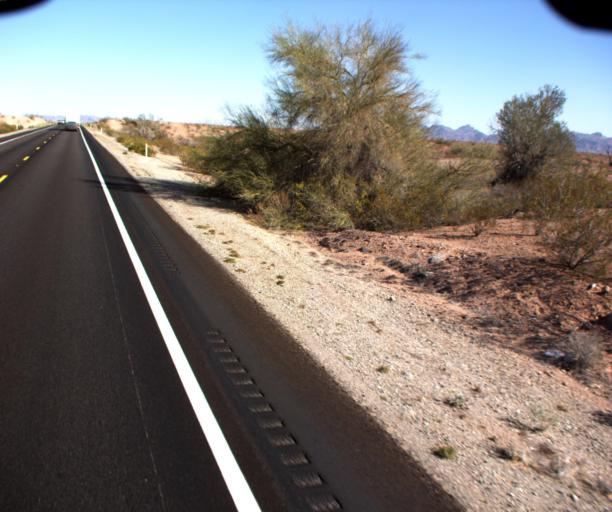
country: US
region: Arizona
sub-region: Yuma County
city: Wellton
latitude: 33.0507
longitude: -114.2912
